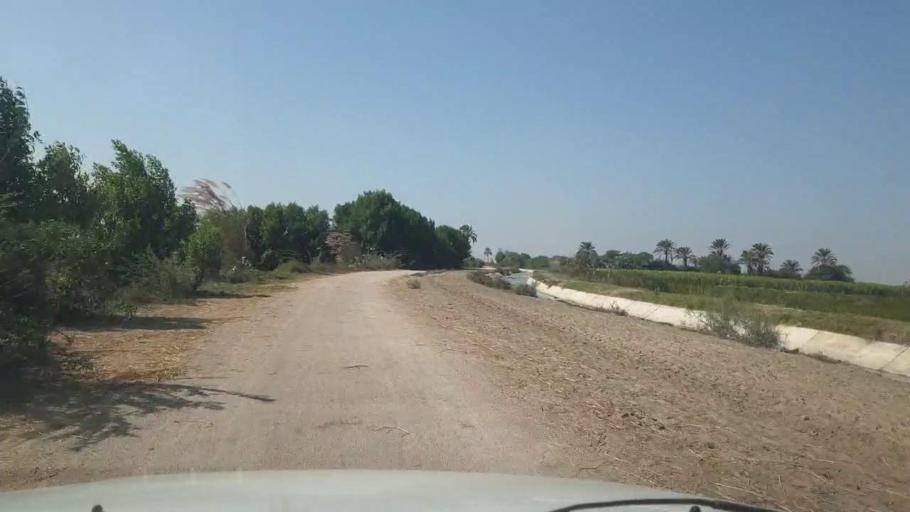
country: PK
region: Sindh
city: Mirpur Sakro
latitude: 24.4183
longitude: 67.7849
